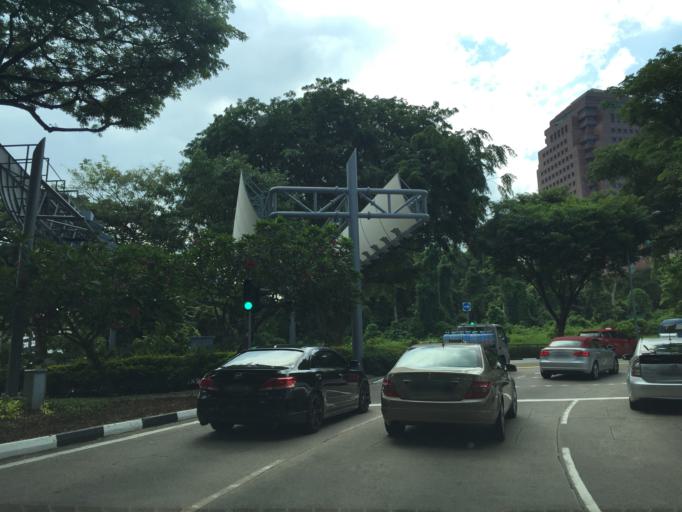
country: SG
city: Singapore
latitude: 1.3005
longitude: 103.8352
